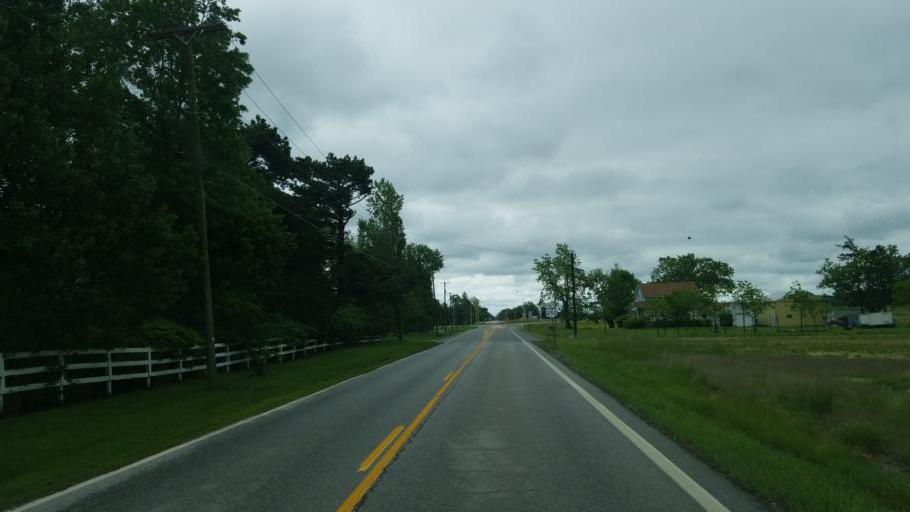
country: US
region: Ohio
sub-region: Medina County
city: Medina
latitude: 41.1808
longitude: -81.9290
